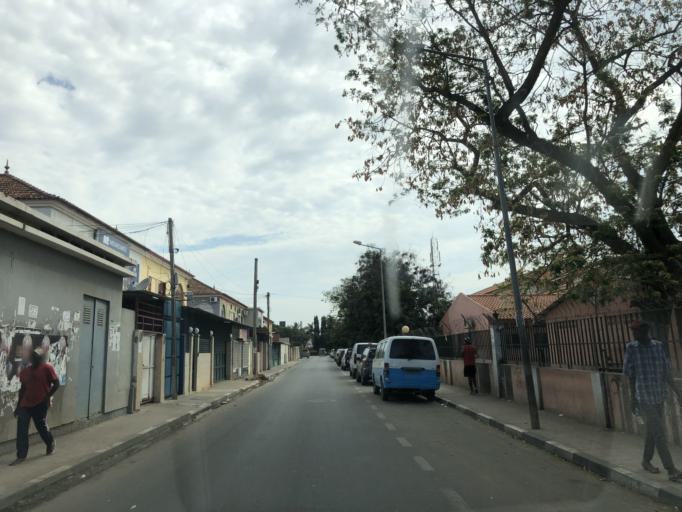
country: AO
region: Luanda
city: Luanda
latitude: -8.8245
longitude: 13.2482
